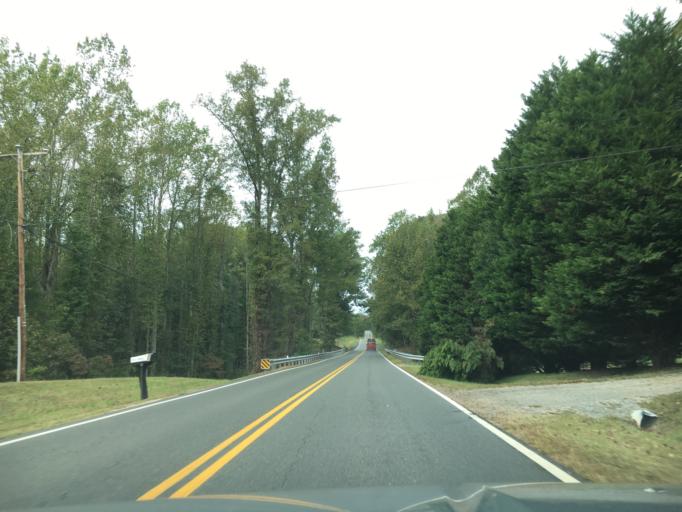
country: US
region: Virginia
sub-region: Goochland County
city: Goochland
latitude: 37.7343
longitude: -77.8396
